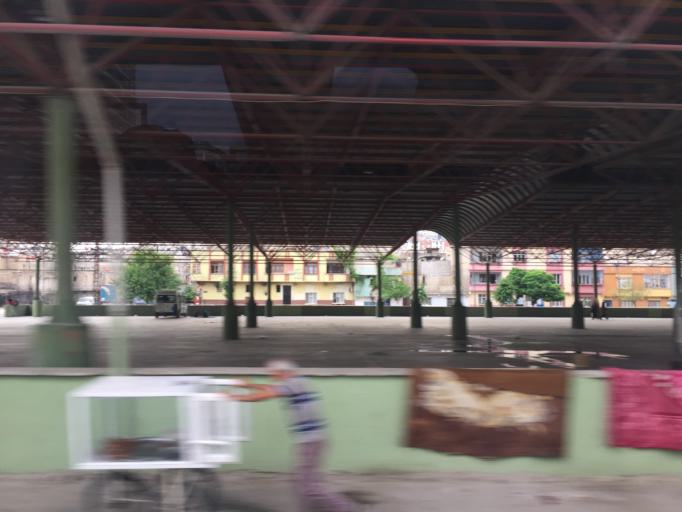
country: TR
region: Gaziantep
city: Gaziantep
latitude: 37.0696
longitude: 37.4138
